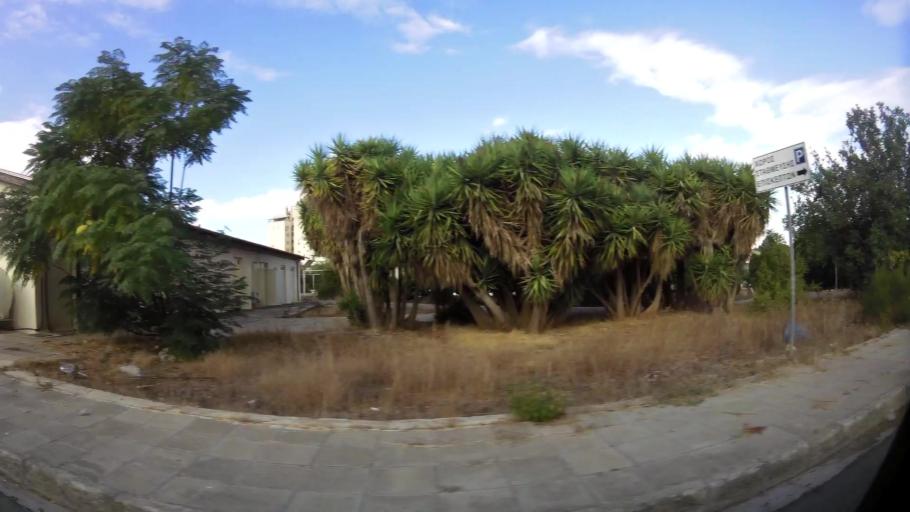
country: CY
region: Lefkosia
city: Nicosia
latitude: 35.1498
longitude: 33.3578
